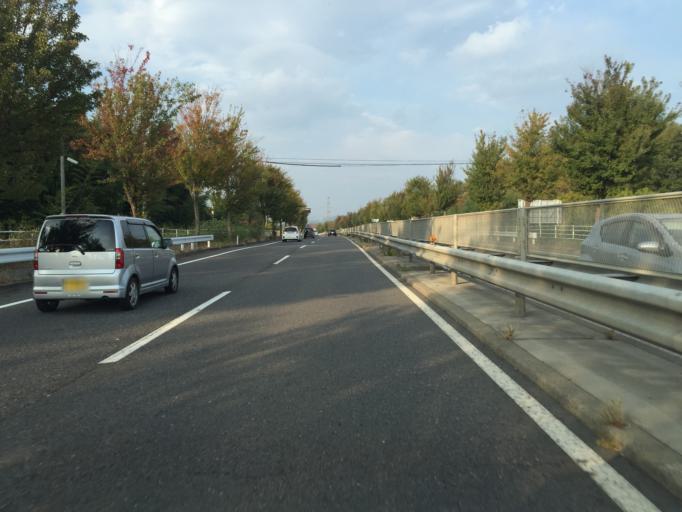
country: JP
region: Fukushima
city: Nihommatsu
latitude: 37.6407
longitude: 140.4848
